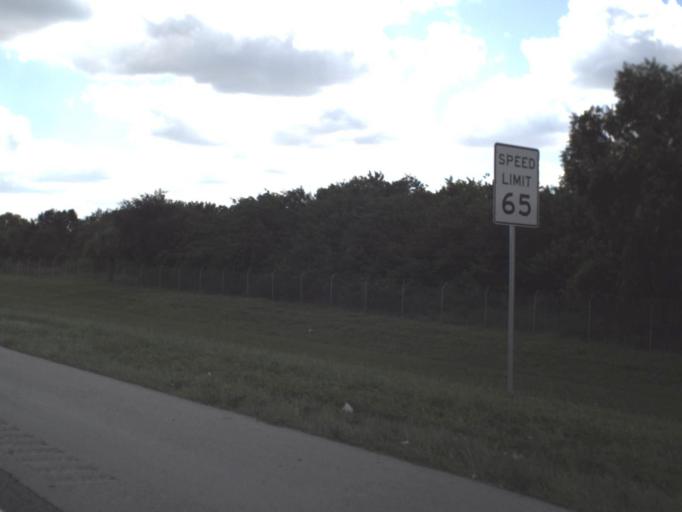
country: US
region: Florida
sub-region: Broward County
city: Coconut Creek
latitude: 26.2636
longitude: -80.1685
